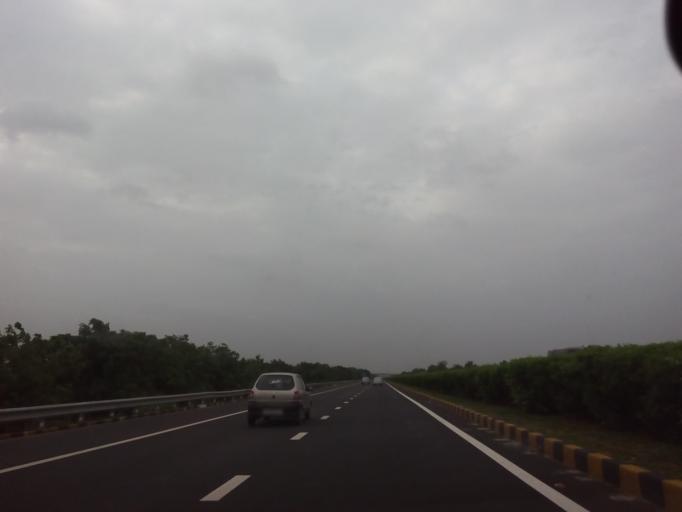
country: IN
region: Gujarat
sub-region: Kheda
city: Chaklasi
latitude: 22.6373
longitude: 72.9410
